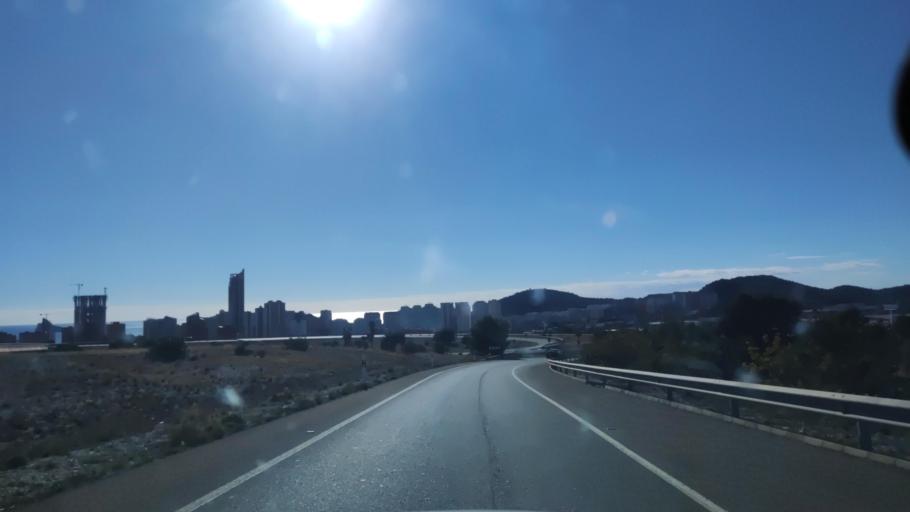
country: ES
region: Valencia
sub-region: Provincia de Alicante
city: Benidorm
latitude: 38.5449
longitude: -0.1719
